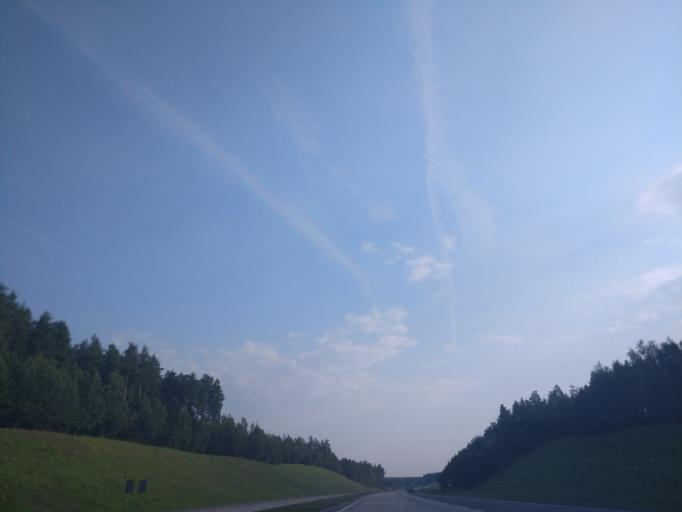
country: BY
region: Minsk
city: Borovlyany
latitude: 54.0279
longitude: 27.6745
